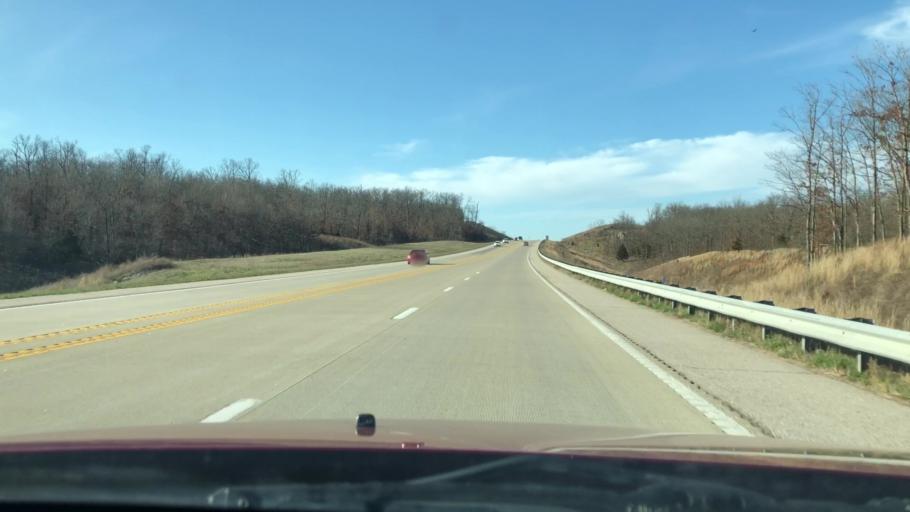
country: US
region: Missouri
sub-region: Camden County
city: Camdenton
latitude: 37.9302
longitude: -92.7137
